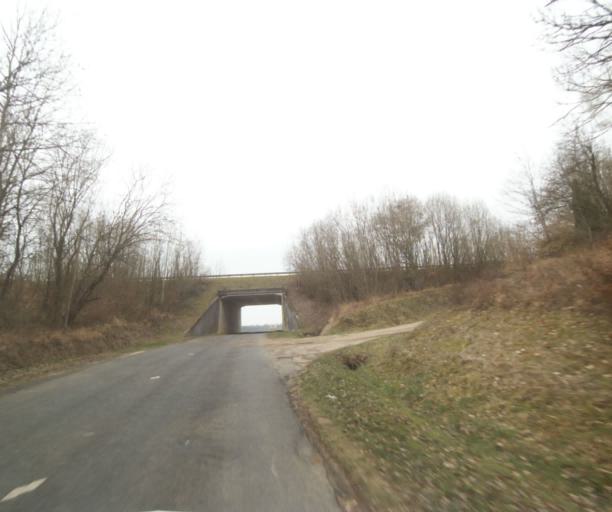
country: FR
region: Champagne-Ardenne
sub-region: Departement de la Haute-Marne
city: Bienville
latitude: 48.5793
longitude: 5.0331
